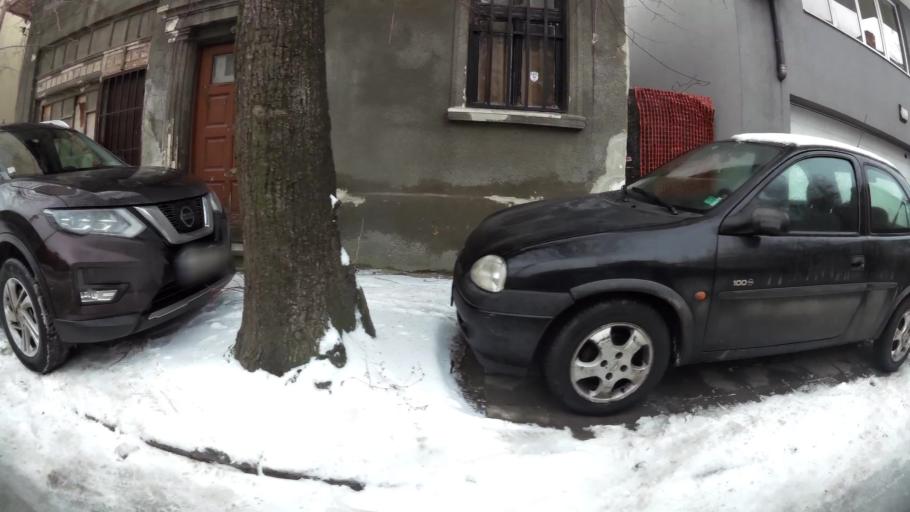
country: BG
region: Sofia-Capital
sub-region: Stolichna Obshtina
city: Sofia
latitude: 42.7068
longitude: 23.3100
